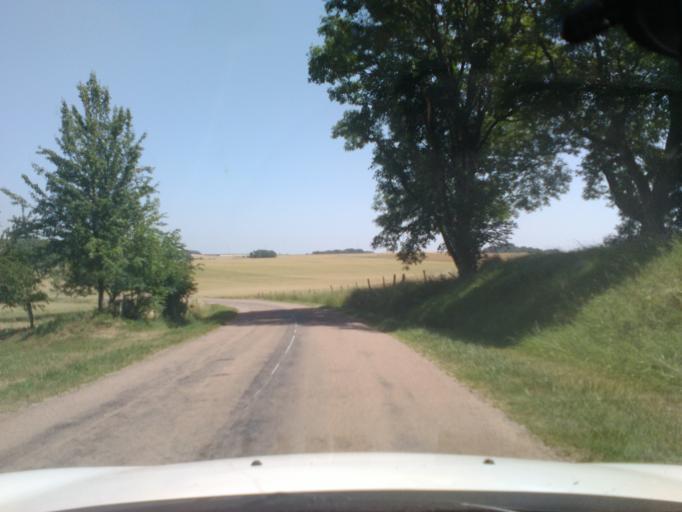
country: FR
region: Lorraine
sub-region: Departement de la Meuse
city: Gondrecourt-le-Chateau
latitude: 48.4229
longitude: 5.5295
